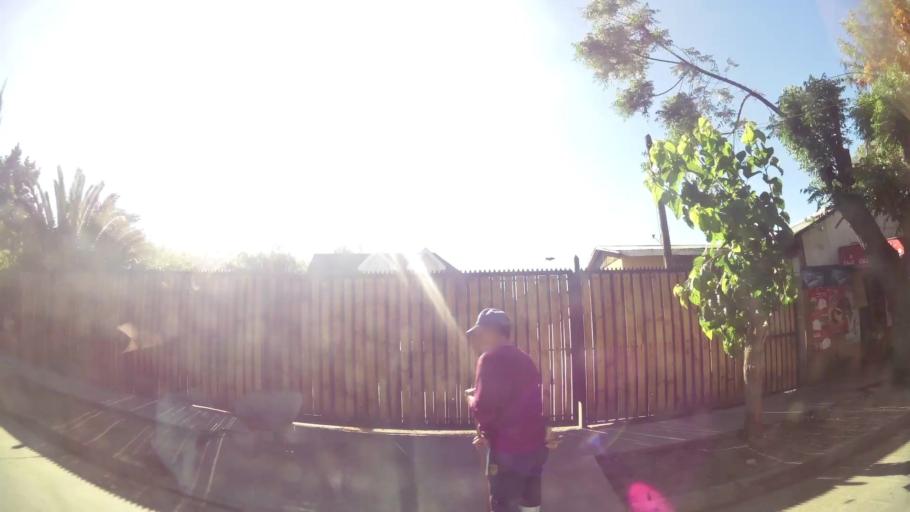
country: CL
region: Santiago Metropolitan
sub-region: Provincia de Chacabuco
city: Lampa
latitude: -33.3968
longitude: -71.1246
